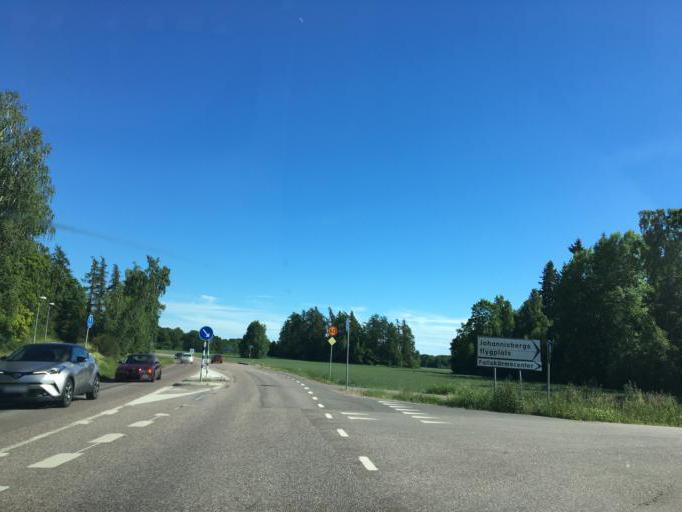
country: SE
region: Vaestmanland
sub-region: Vasteras
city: Vasteras
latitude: 59.5845
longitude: 16.5044
